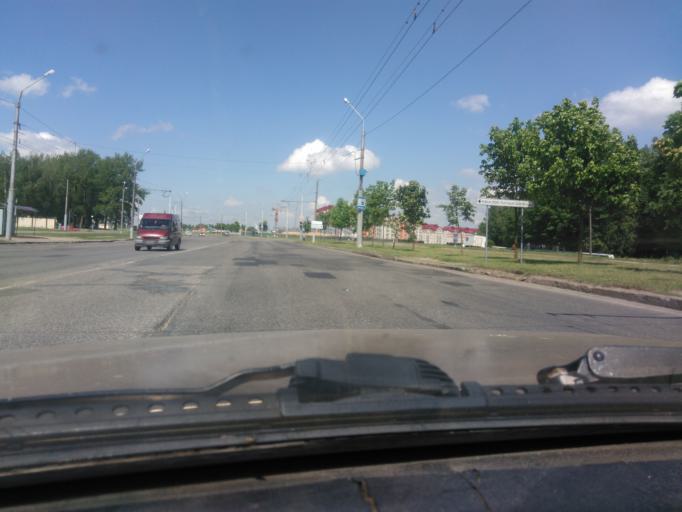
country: BY
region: Mogilev
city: Palykavichy Pyershyya
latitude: 53.9582
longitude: 30.3630
